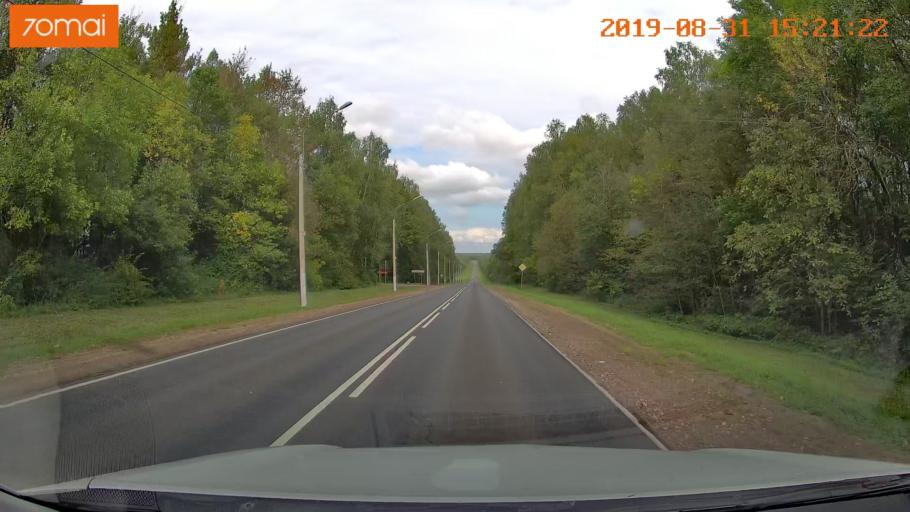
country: RU
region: Kaluga
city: Baryatino
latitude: 54.4957
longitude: 34.4521
